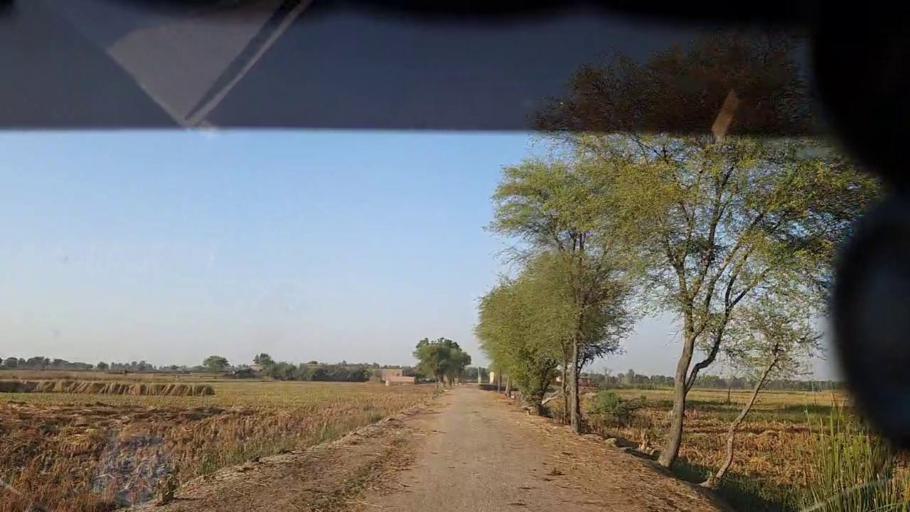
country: PK
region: Sindh
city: Ratodero
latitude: 27.8686
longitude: 68.1987
